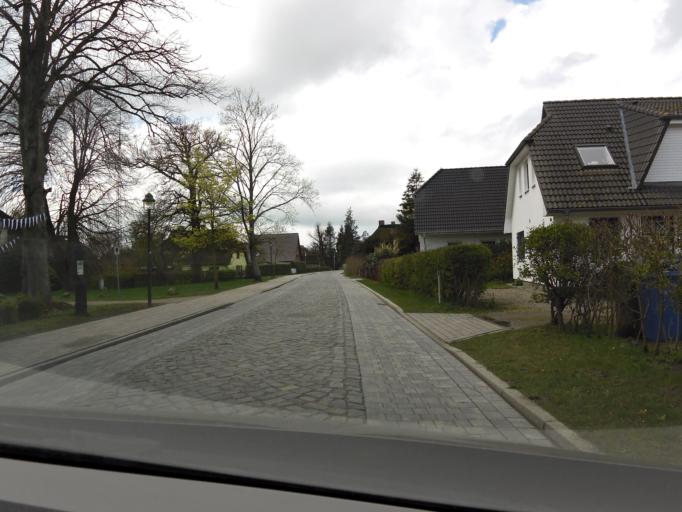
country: DE
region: Mecklenburg-Vorpommern
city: Born
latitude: 54.3830
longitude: 12.5307
